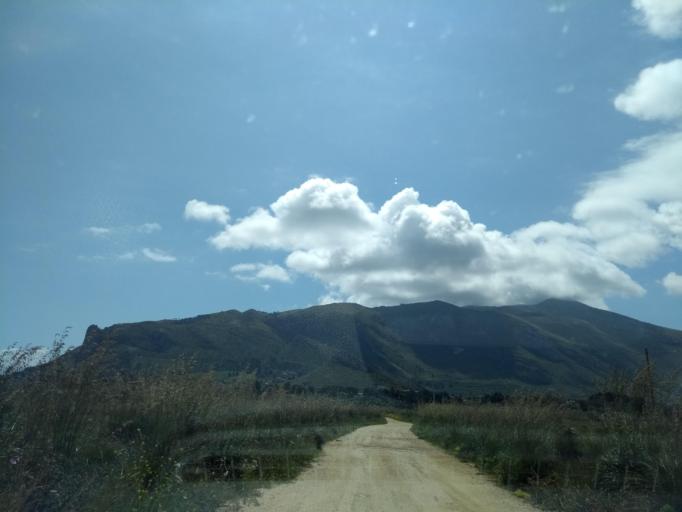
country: IT
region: Sicily
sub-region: Trapani
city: Castellammare del Golfo
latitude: 38.0469
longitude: 12.8481
